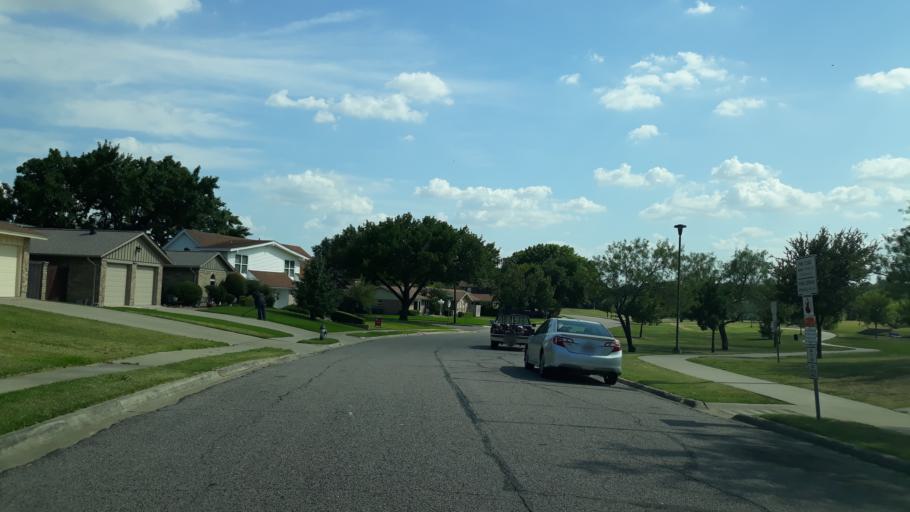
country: US
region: Texas
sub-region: Dallas County
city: Irving
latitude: 32.8453
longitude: -96.9989
